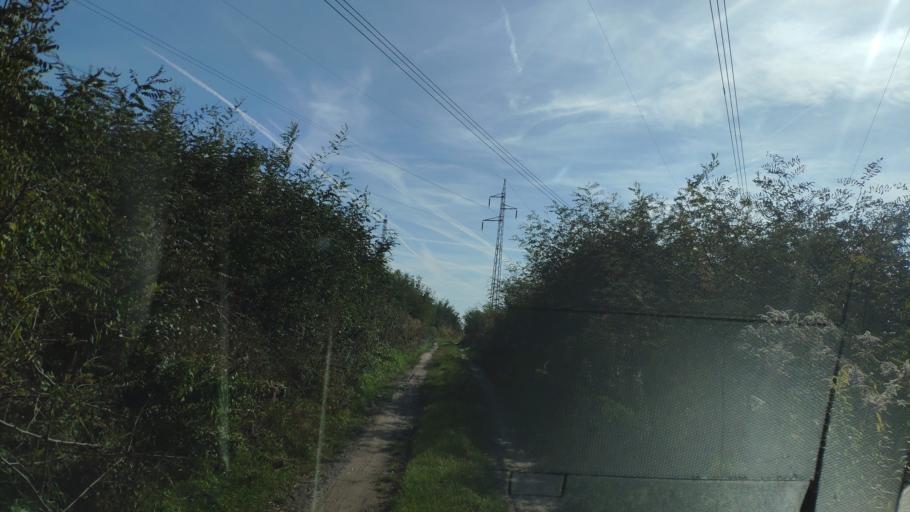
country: SK
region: Presovsky
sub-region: Okres Presov
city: Presov
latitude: 48.8825
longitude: 21.2327
